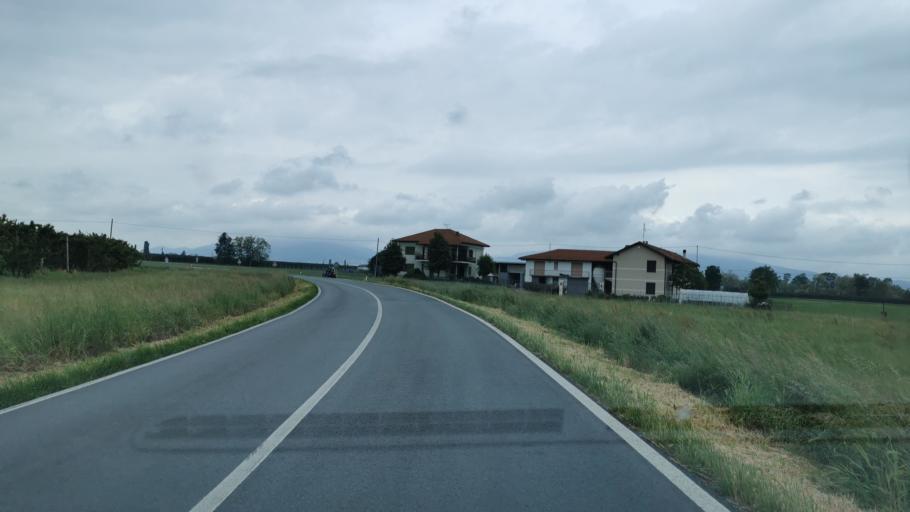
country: IT
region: Piedmont
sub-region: Provincia di Cuneo
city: Lagnasco
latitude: 44.6037
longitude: 7.5722
